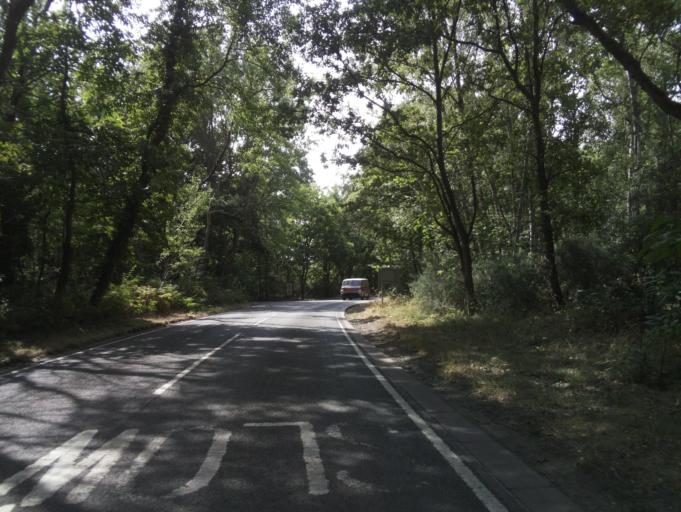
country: GB
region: England
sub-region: Surrey
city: Pirbright
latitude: 51.3128
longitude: -0.6468
